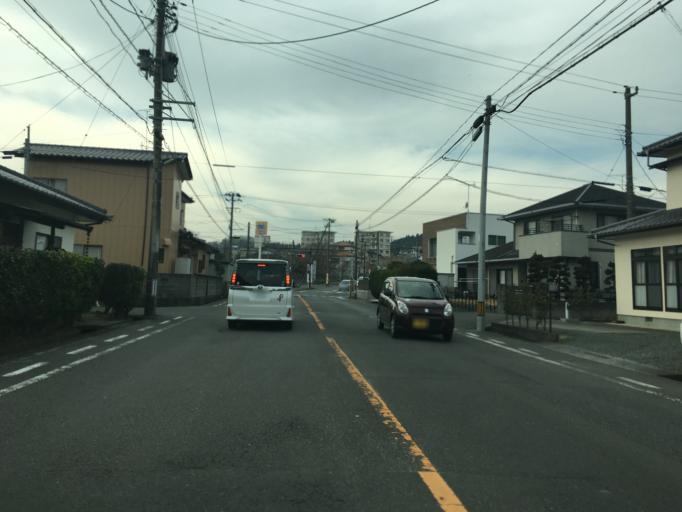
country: JP
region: Fukushima
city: Iwaki
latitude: 36.9843
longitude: 140.8875
